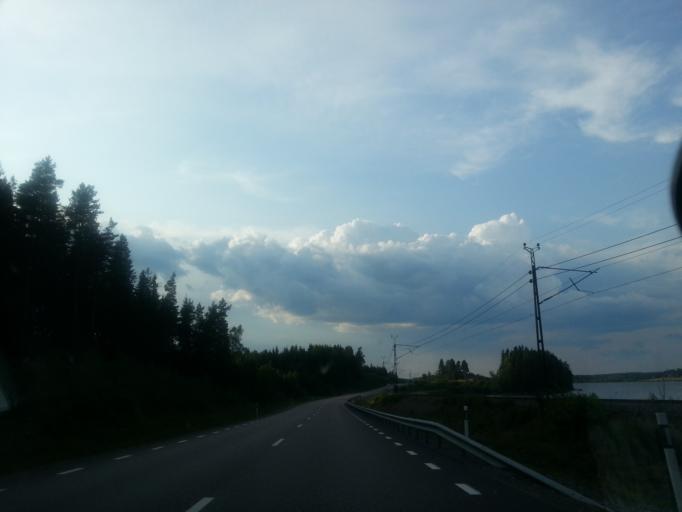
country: SE
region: Dalarna
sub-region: Avesta Kommun
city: Horndal
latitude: 60.3230
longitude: 16.4157
